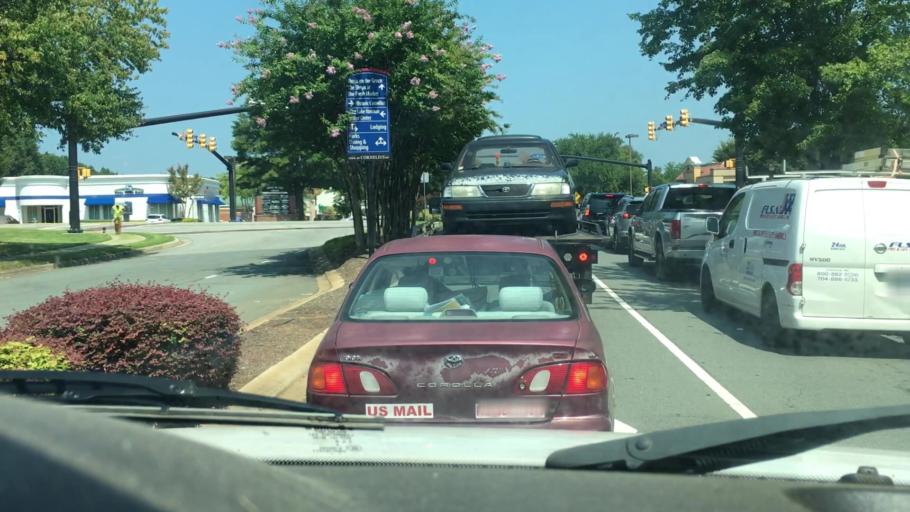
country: US
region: North Carolina
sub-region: Mecklenburg County
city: Cornelius
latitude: 35.4825
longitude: -80.8777
